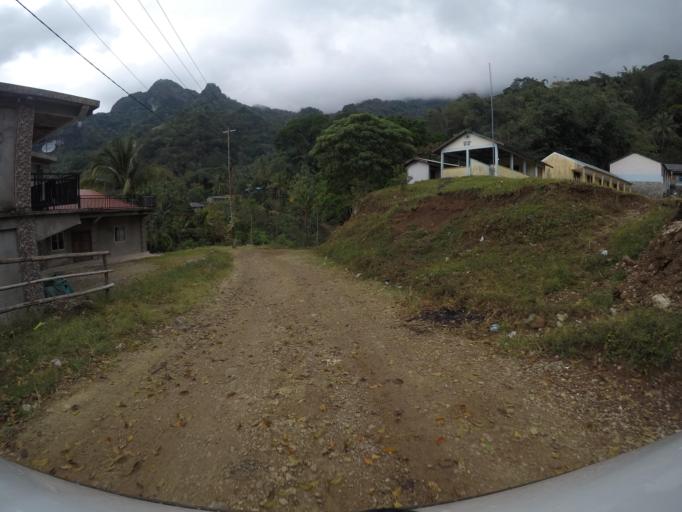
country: TL
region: Baucau
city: Baucau
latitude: -8.6460
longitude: 126.6301
